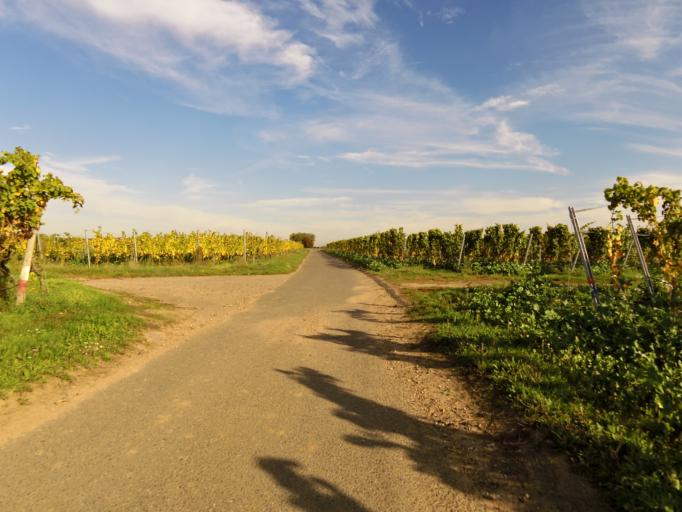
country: DE
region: Rheinland-Pfalz
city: Friedelsheim
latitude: 49.4419
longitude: 8.2047
